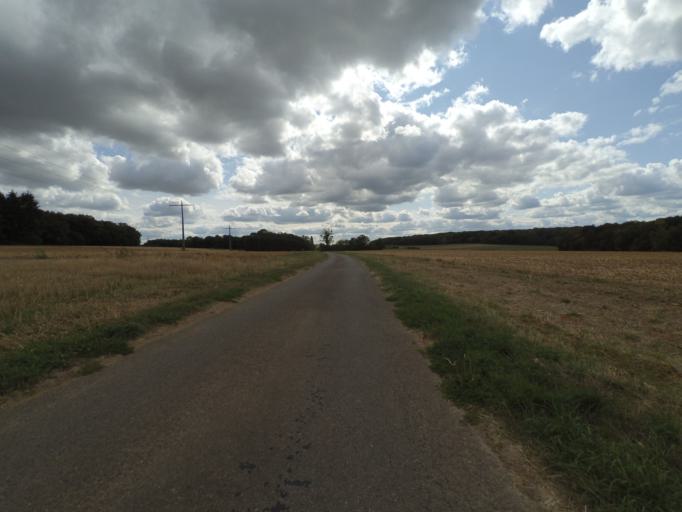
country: LU
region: Luxembourg
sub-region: Canton de Luxembourg
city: Weiler-la-Tour
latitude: 49.5620
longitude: 6.2077
